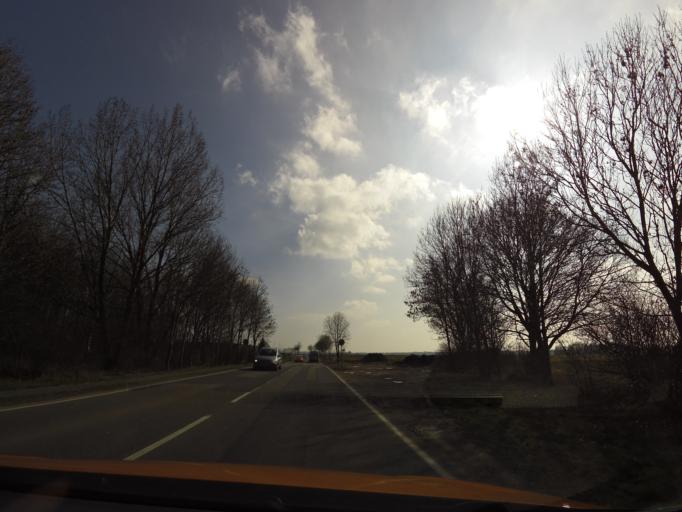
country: DE
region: Lower Saxony
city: Brake (Unterweser)
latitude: 53.3235
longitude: 8.4602
